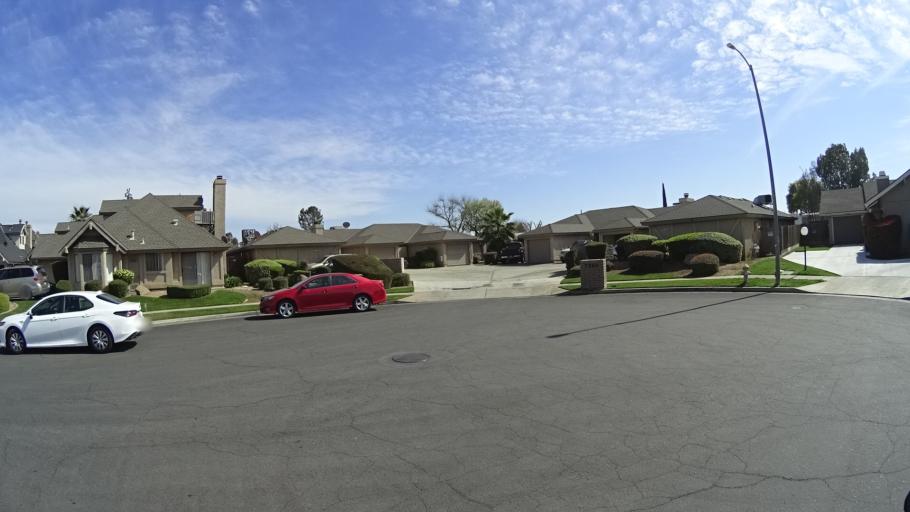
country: US
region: California
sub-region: Fresno County
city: Clovis
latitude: 36.8479
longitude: -119.7832
